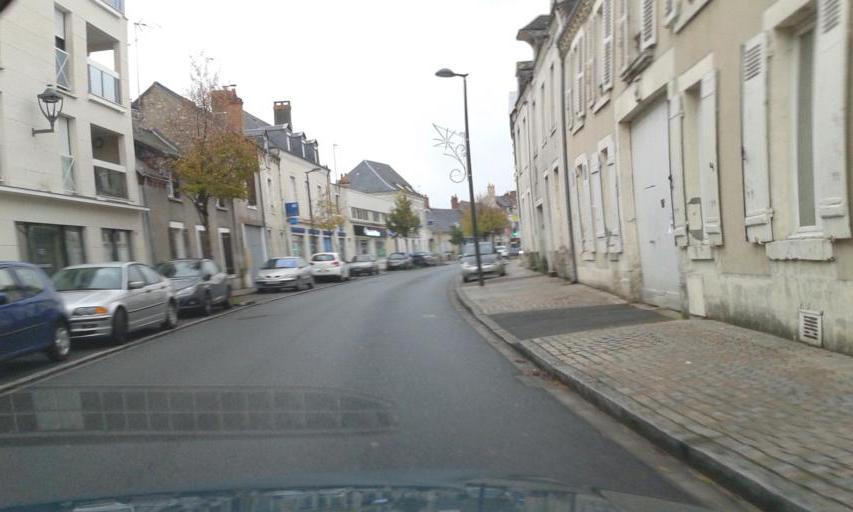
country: FR
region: Centre
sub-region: Departement du Loiret
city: Olivet
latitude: 47.8620
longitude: 1.9003
